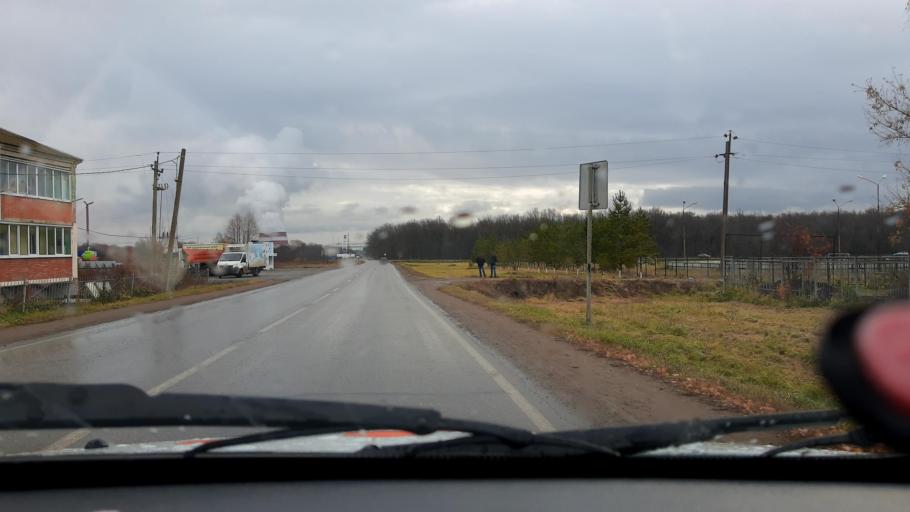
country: RU
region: Bashkortostan
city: Mikhaylovka
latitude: 54.8104
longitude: 55.8105
